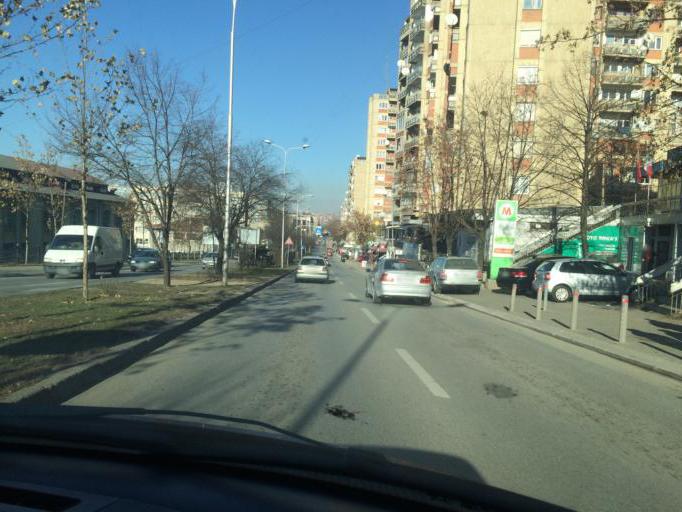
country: XK
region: Pristina
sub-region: Komuna e Prishtines
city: Pristina
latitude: 42.6557
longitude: 21.1642
